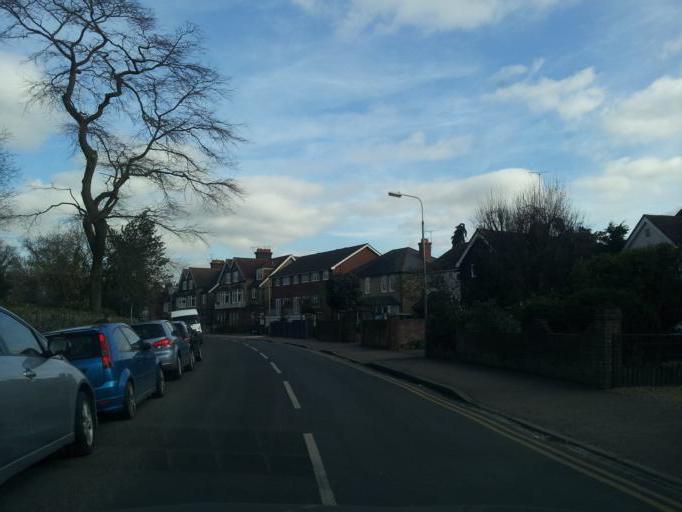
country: GB
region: England
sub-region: Hertfordshire
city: St Albans
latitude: 51.7533
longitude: -0.3213
